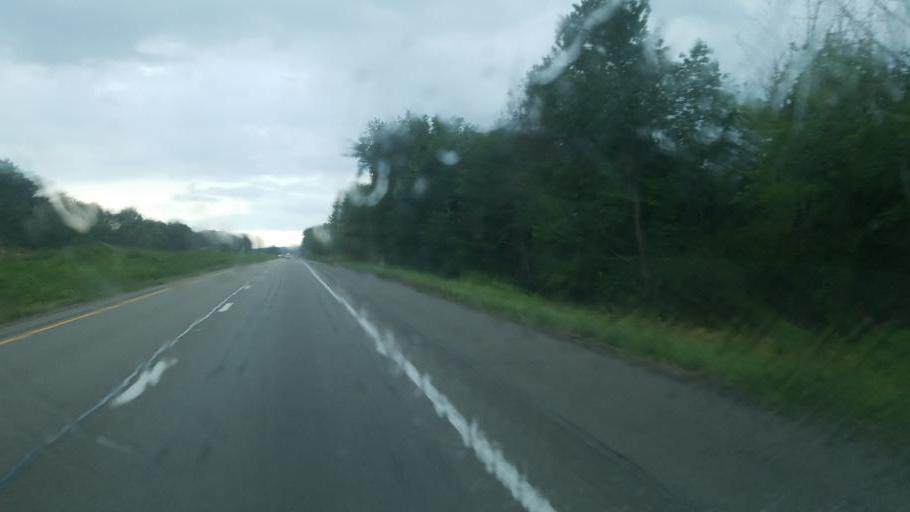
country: US
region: Pennsylvania
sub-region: Mercer County
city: Grove City
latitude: 41.1719
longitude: -80.1658
